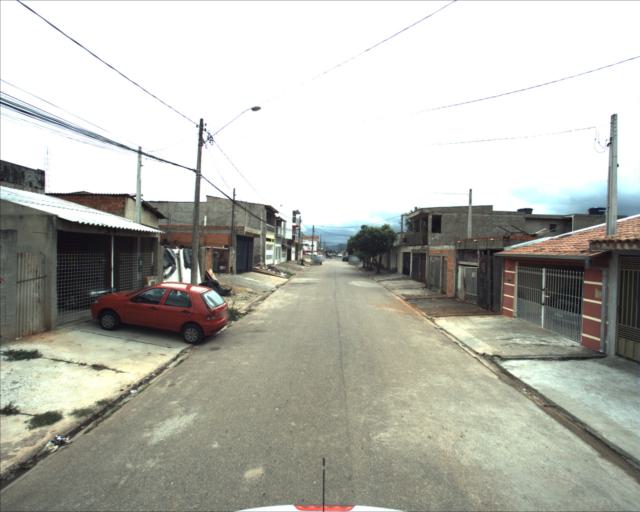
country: BR
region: Sao Paulo
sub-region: Sorocaba
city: Sorocaba
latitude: -23.4324
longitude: -47.5059
